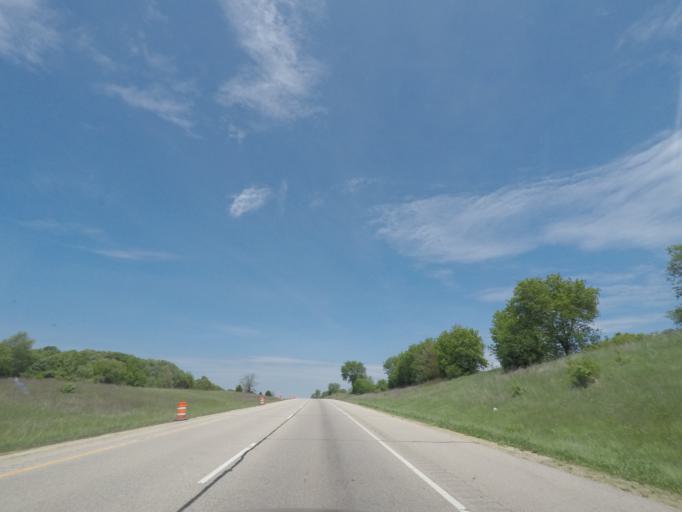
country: US
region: Wisconsin
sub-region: Dane County
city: Oregon
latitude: 42.9736
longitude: -89.3858
